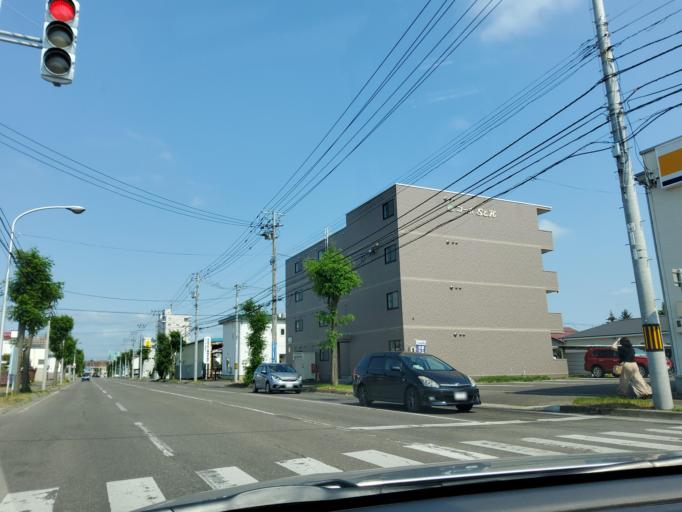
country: JP
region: Hokkaido
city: Obihiro
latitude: 42.9161
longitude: 143.1935
